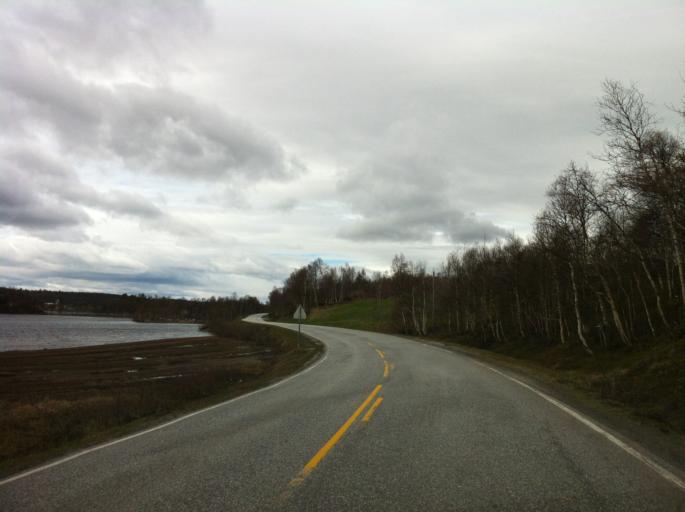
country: NO
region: Sor-Trondelag
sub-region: Roros
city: Roros
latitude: 62.6017
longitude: 11.5436
